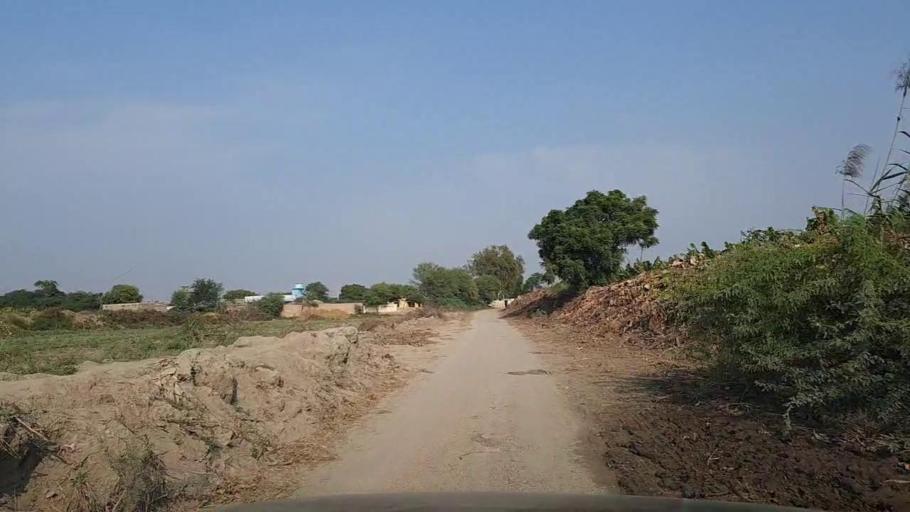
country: PK
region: Sindh
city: Thatta
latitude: 24.6453
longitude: 67.9329
